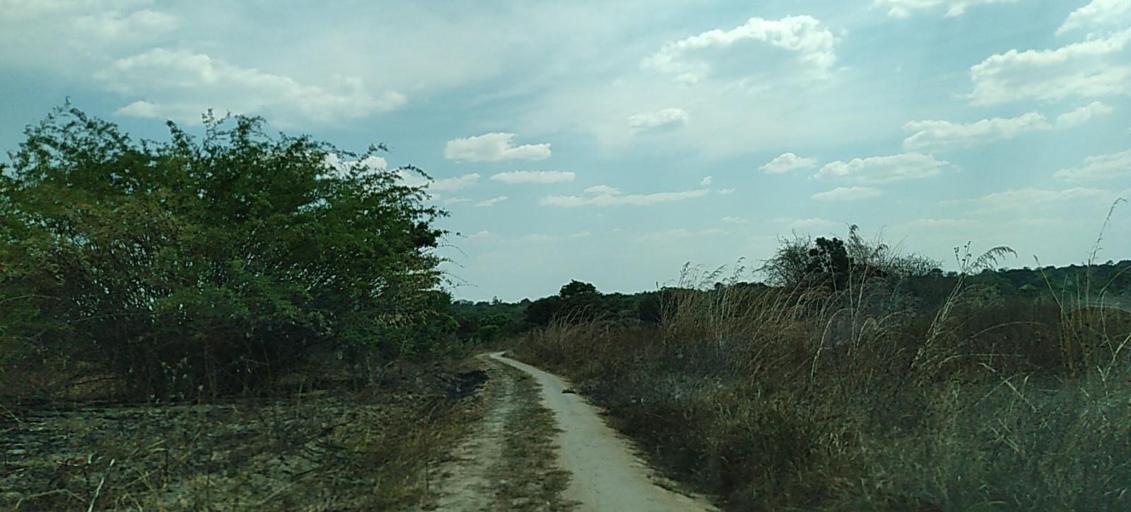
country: ZM
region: Copperbelt
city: Chililabombwe
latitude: -12.3333
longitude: 27.7856
